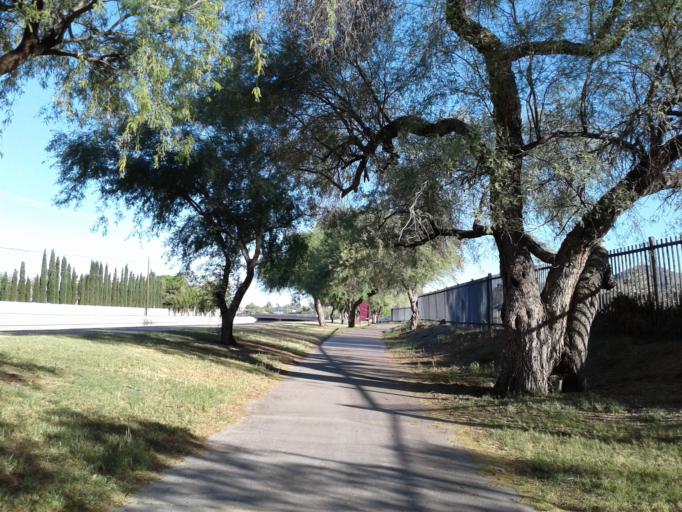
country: US
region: Arizona
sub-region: Maricopa County
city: Glendale
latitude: 33.5660
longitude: -112.0782
